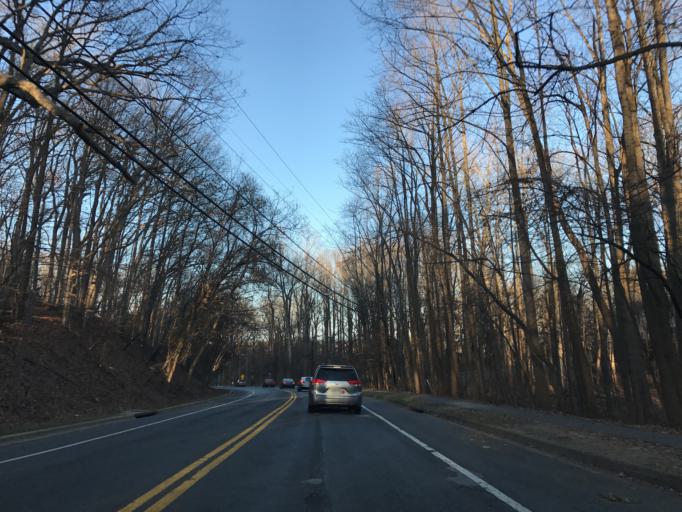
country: US
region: Maryland
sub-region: Montgomery County
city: Kemp Mill
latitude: 39.0546
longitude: -77.0241
